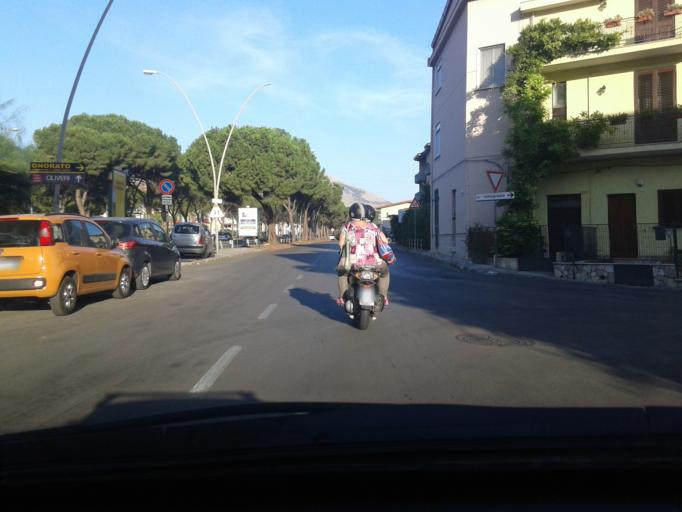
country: IT
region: Sicily
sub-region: Palermo
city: Villa Ciambra
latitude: 38.0868
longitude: 13.3502
